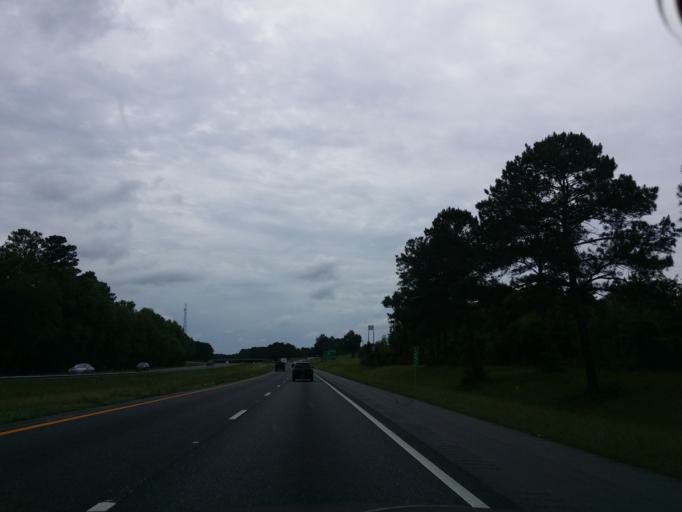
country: US
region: Florida
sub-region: Madison County
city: Madison
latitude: 30.4273
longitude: -83.4496
